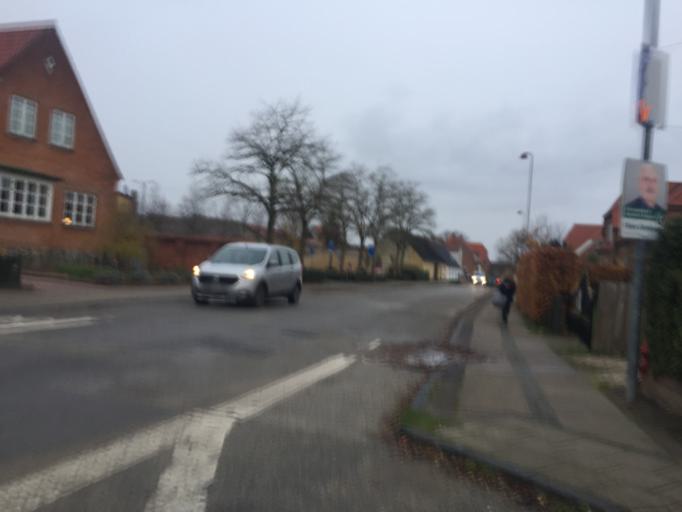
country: DK
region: Zealand
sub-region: Ringsted Kommune
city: Ringsted
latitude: 55.4470
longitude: 11.7909
